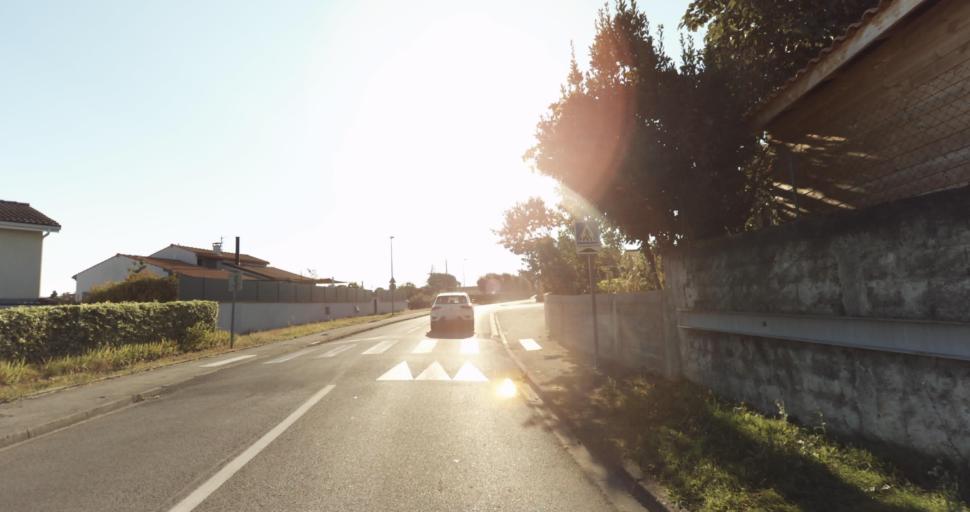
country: FR
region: Midi-Pyrenees
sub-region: Departement de la Haute-Garonne
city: L'Union
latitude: 43.6636
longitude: 1.4765
